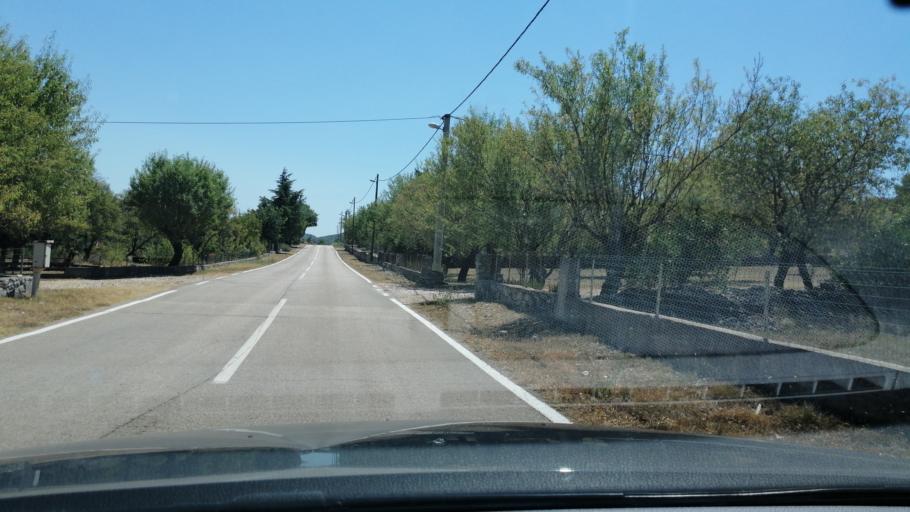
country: HR
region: Sibensko-Kniniska
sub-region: Grad Sibenik
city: Pirovac
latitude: 43.8698
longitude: 15.6804
